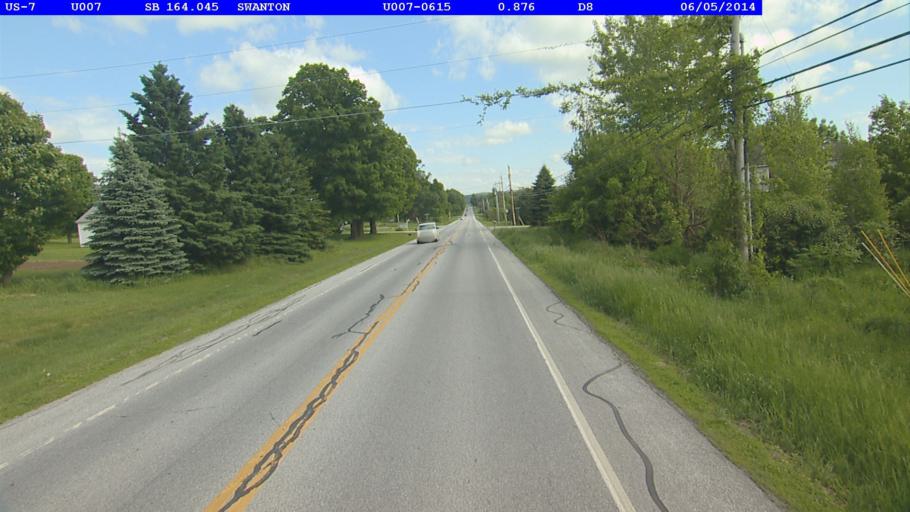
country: US
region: Vermont
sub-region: Franklin County
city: Saint Albans
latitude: 44.8605
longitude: -73.0964
